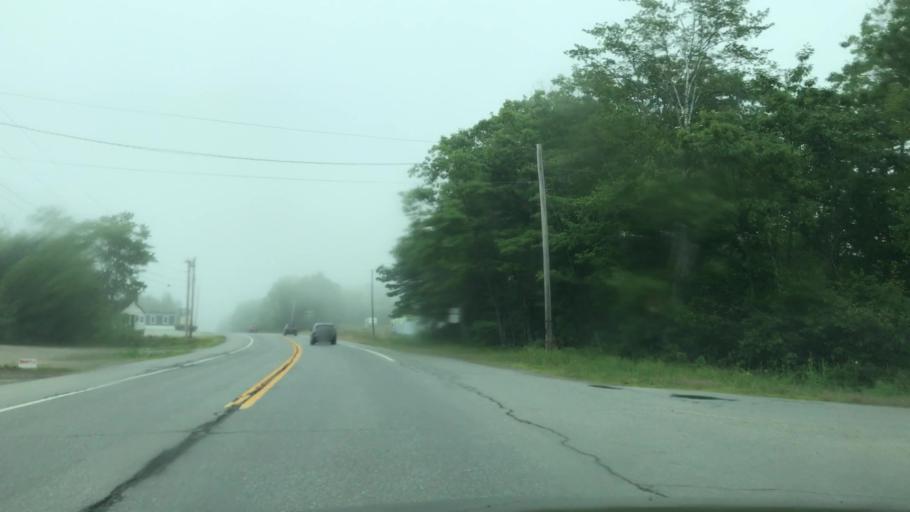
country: US
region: Maine
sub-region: Lincoln County
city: Waldoboro
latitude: 44.0984
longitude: -69.4086
